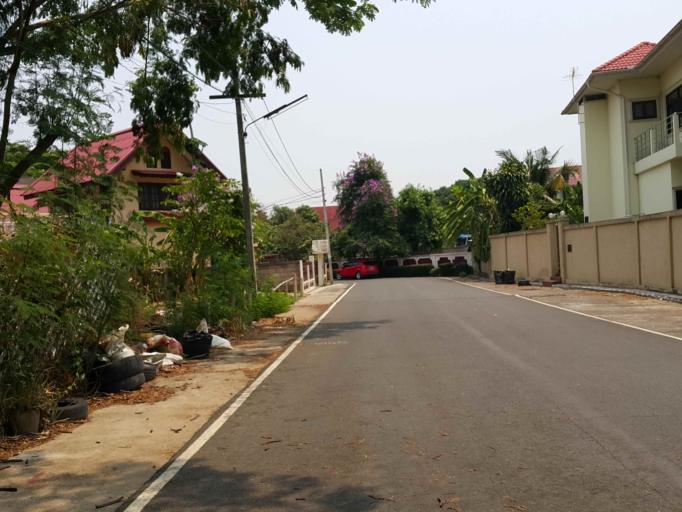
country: TH
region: Chiang Mai
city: Chiang Mai
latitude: 18.7569
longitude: 99.0102
